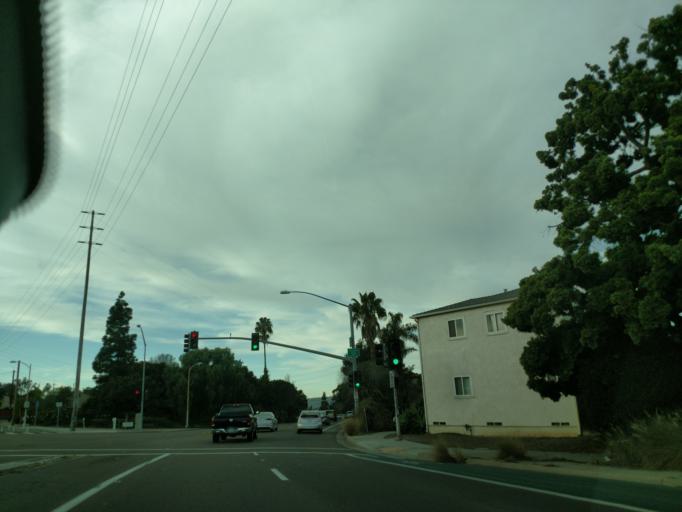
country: US
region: California
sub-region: San Diego County
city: Coronado
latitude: 32.7392
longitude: -117.2314
